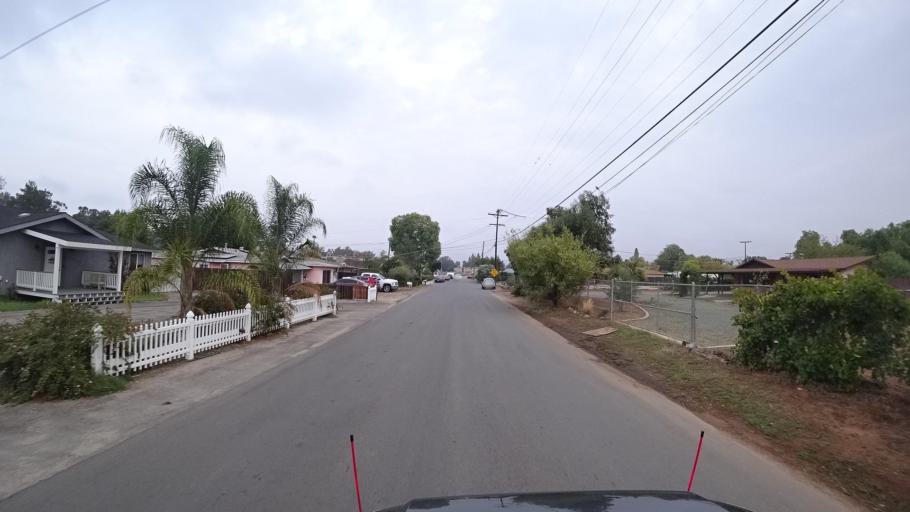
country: US
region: California
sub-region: San Diego County
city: Ramona
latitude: 33.0326
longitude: -116.8807
